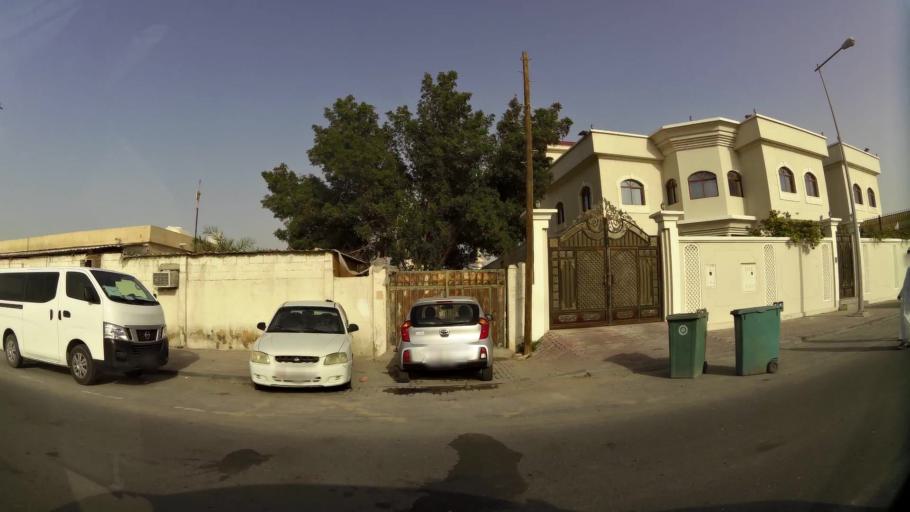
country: QA
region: Baladiyat ar Rayyan
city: Ar Rayyan
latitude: 25.2333
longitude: 51.4368
